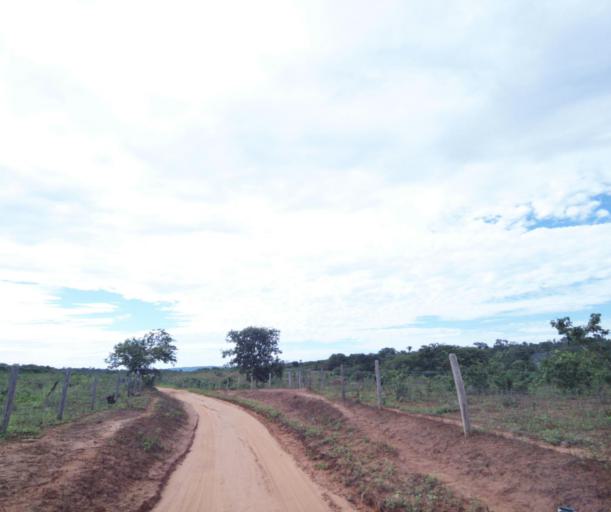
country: BR
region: Bahia
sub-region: Carinhanha
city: Carinhanha
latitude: -14.2190
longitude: -44.4429
